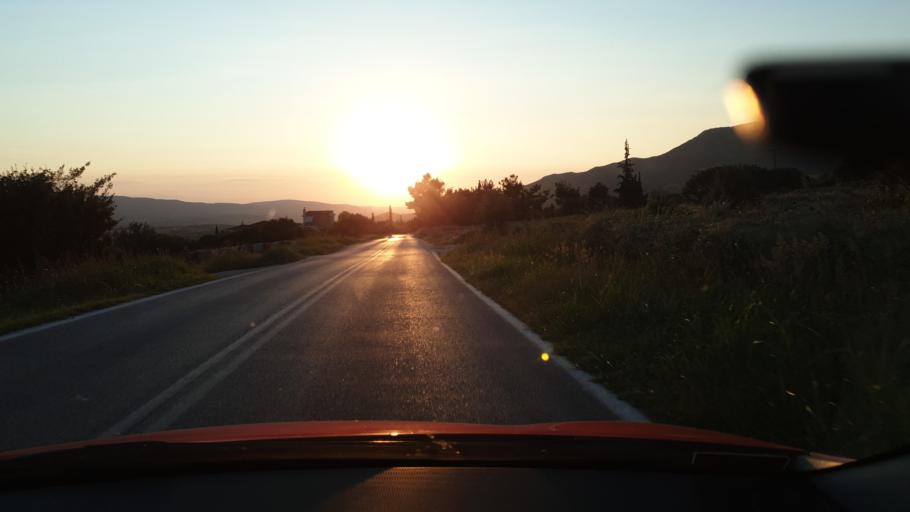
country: GR
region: Central Macedonia
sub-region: Nomos Chalkidikis
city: Galatista
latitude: 40.4678
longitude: 23.2621
